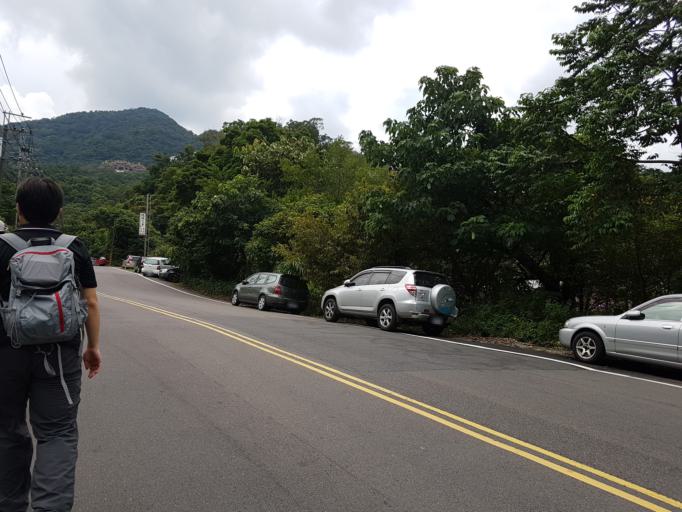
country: TW
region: Taiwan
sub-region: Keelung
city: Keelung
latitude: 25.0586
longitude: 121.6609
